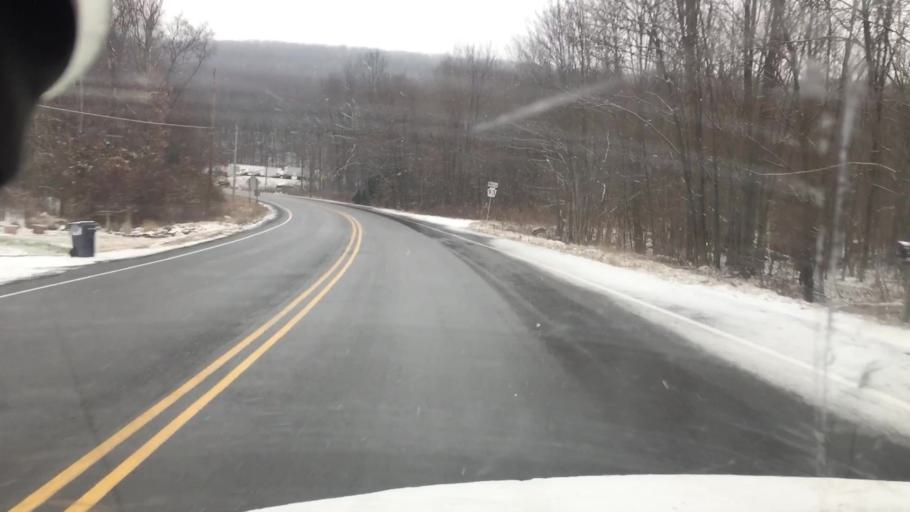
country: US
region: Pennsylvania
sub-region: Luzerne County
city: Conyngham
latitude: 41.0289
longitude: -76.0790
